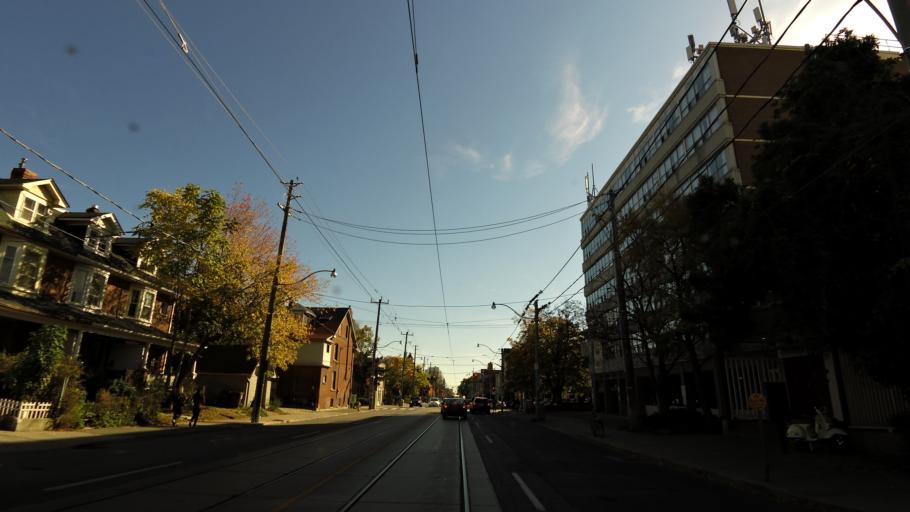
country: CA
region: Ontario
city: Toronto
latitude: 43.6687
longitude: -79.4126
